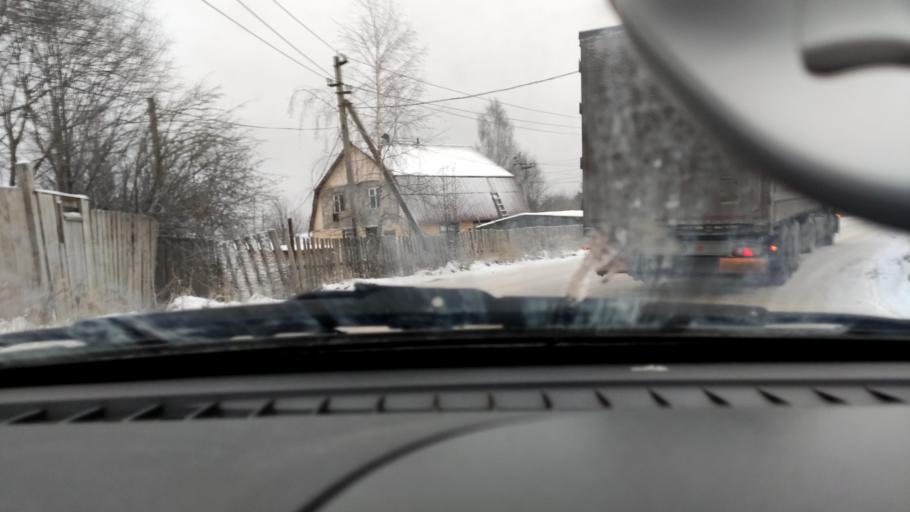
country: RU
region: Perm
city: Polazna
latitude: 58.1785
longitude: 56.4115
